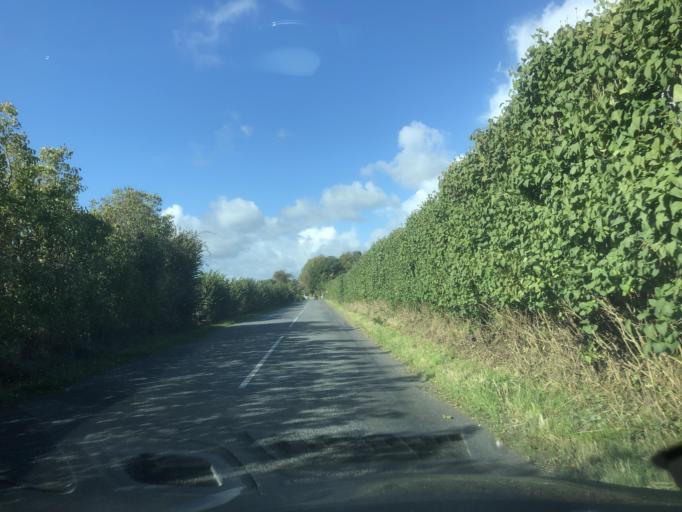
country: DK
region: South Denmark
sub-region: Faaborg-Midtfyn Kommune
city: Ringe
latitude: 55.2448
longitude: 10.3766
